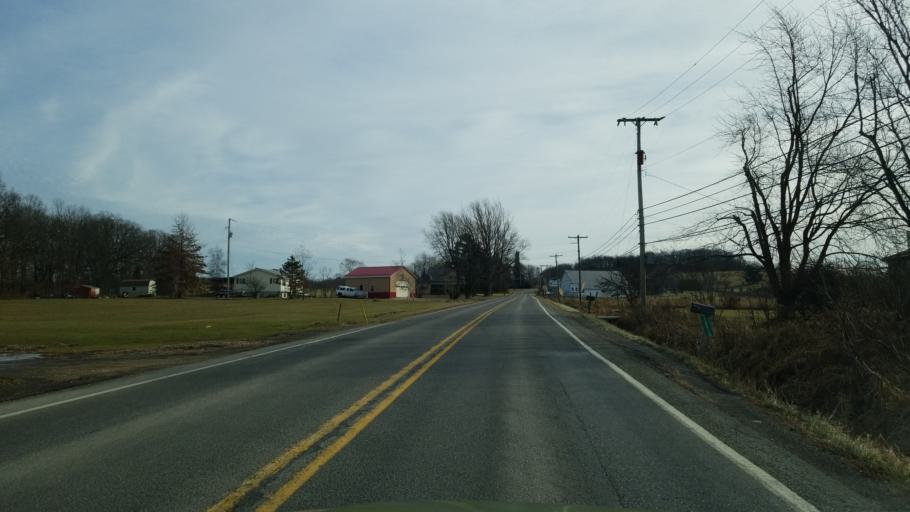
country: US
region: Pennsylvania
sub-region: Indiana County
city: Johnsonburg
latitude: 40.9242
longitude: -78.8687
